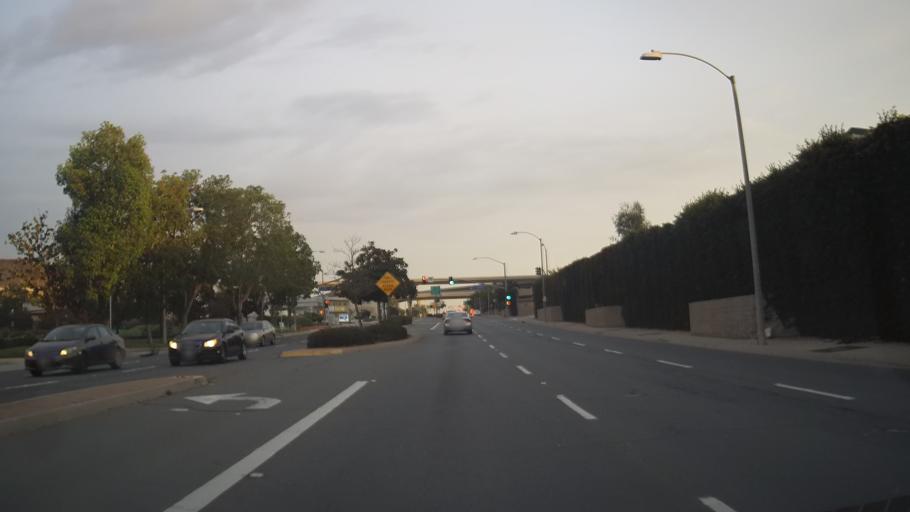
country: US
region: California
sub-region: San Diego County
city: Santee
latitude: 32.8362
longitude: -116.9662
